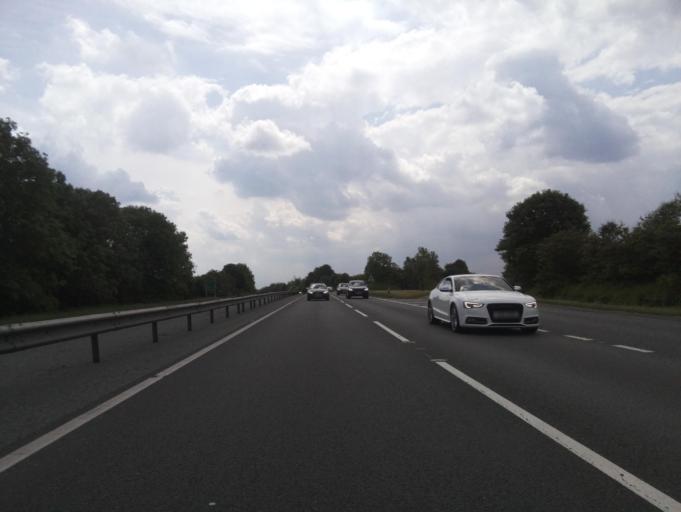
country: GB
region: England
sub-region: North Yorkshire
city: Northallerton
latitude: 54.3686
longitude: -1.3225
